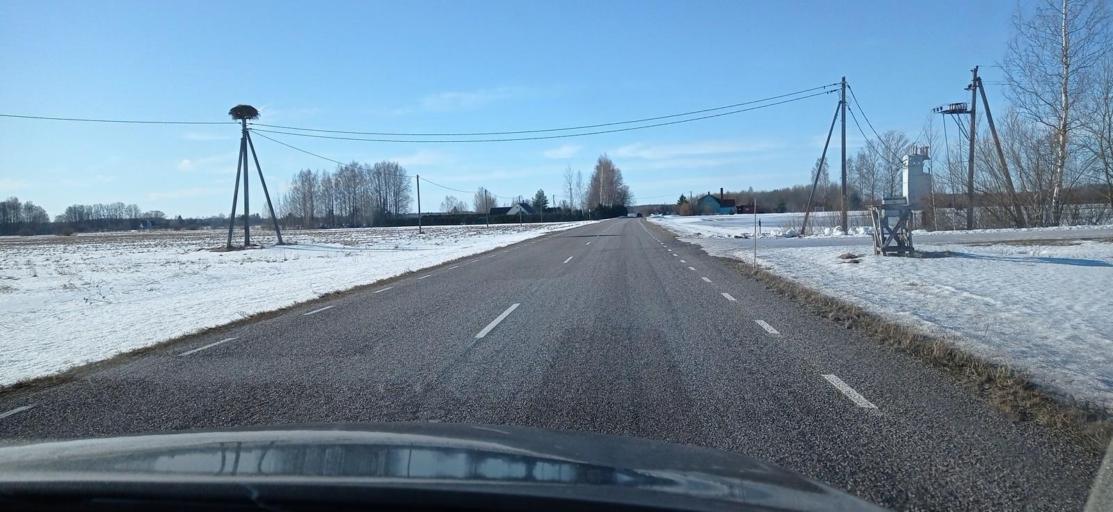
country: EE
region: Tartu
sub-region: Alatskivi vald
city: Kallaste
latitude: 58.4953
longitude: 27.2098
